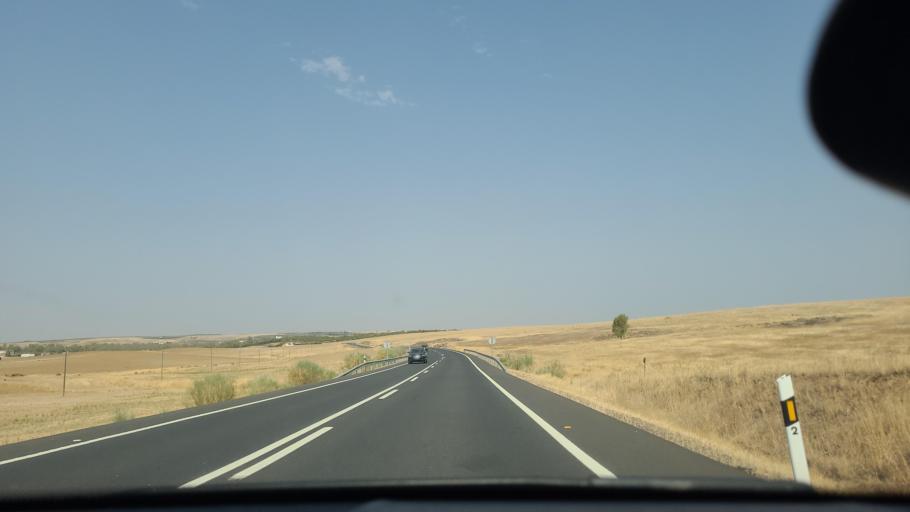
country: ES
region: Extremadura
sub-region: Provincia de Badajoz
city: Berlanga
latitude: 38.2698
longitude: -5.7925
